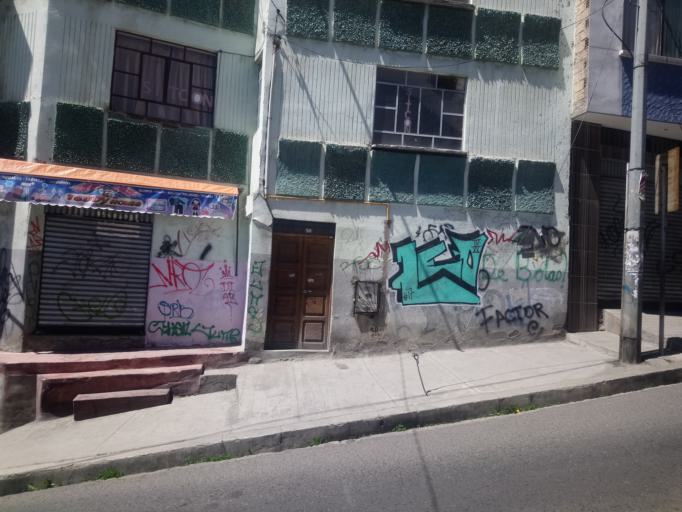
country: BO
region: La Paz
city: La Paz
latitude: -16.4967
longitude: -68.1099
